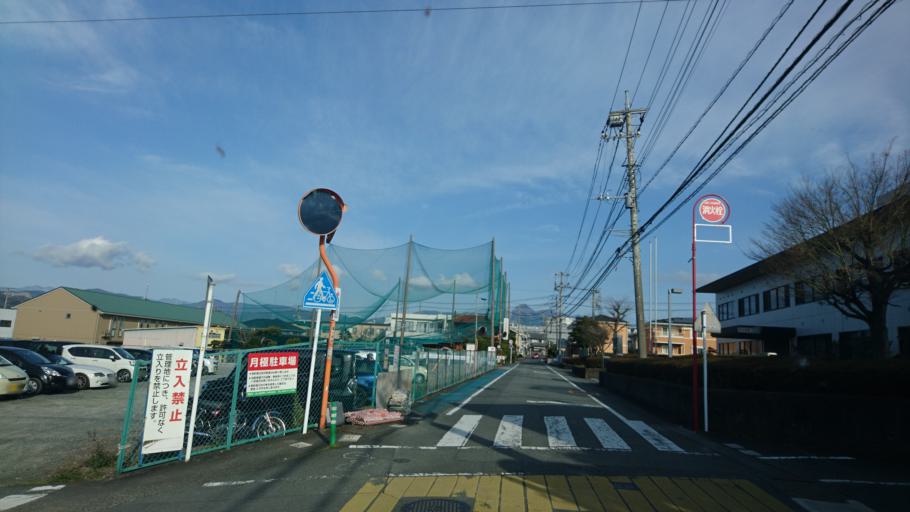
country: JP
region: Shizuoka
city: Fujinomiya
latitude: 35.2402
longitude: 138.6167
